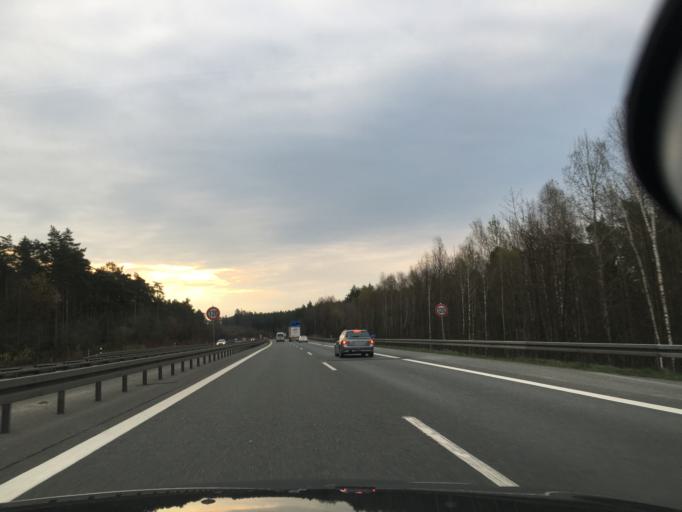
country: DE
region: Bavaria
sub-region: Regierungsbezirk Mittelfranken
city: Winkelhaid
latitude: 49.4019
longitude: 11.2772
